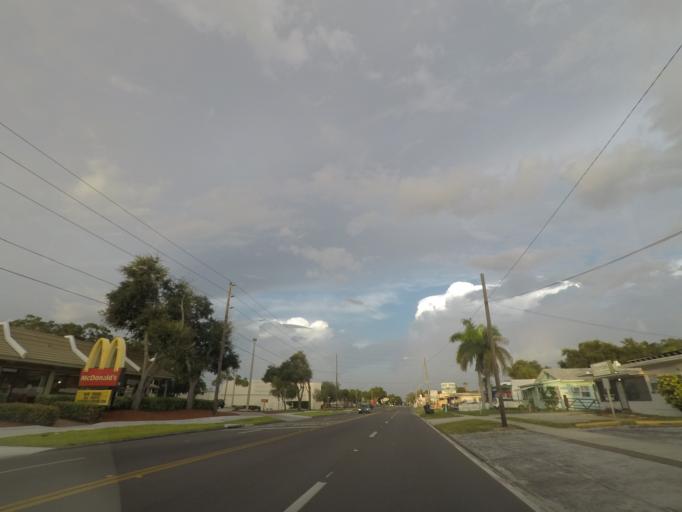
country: US
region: Florida
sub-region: Pinellas County
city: Gulfport
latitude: 27.7483
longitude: -82.7027
